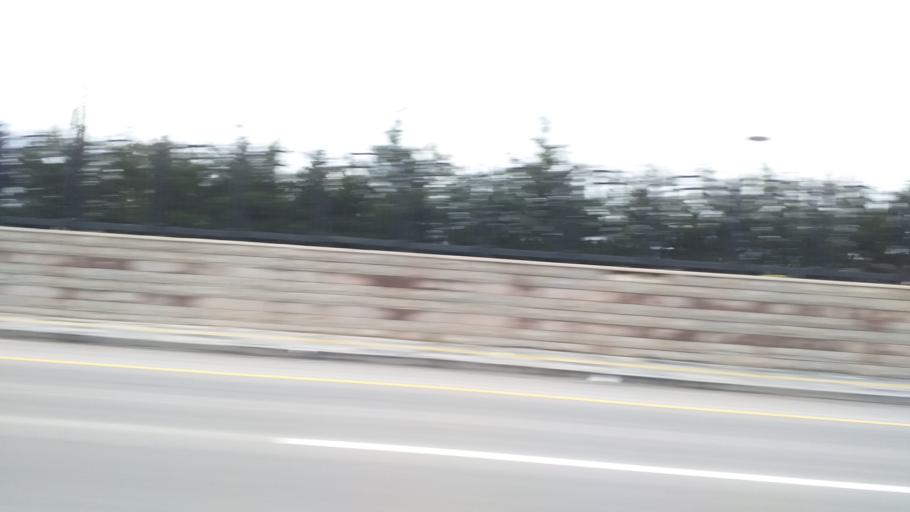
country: TR
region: Ankara
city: Ankara
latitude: 39.9292
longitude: 32.8125
